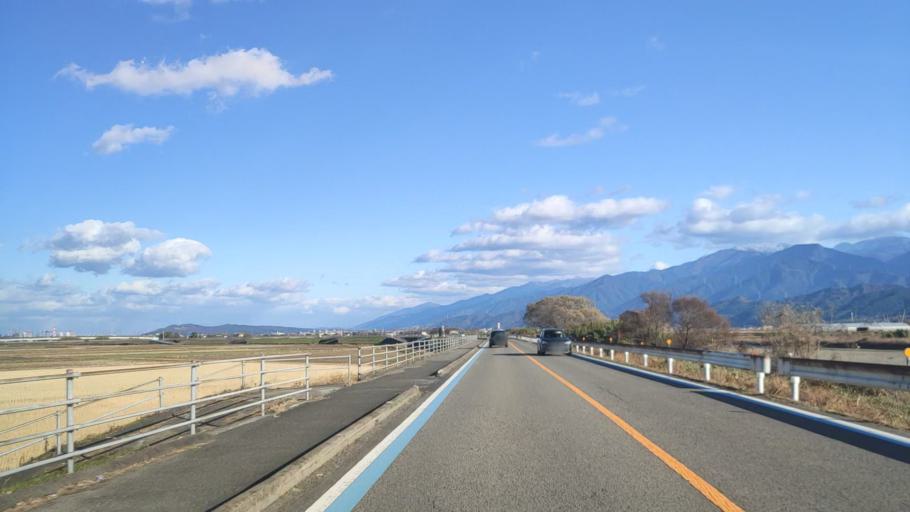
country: JP
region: Ehime
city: Saijo
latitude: 33.9068
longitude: 133.1213
